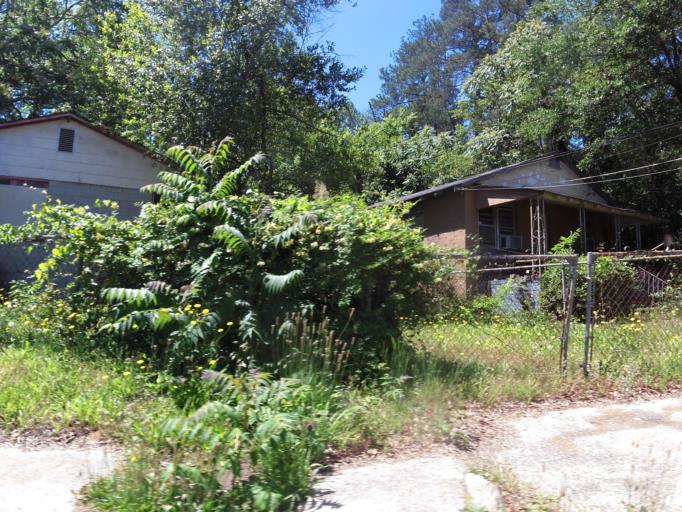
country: US
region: Georgia
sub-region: Richmond County
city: Augusta
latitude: 33.4837
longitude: -82.0258
